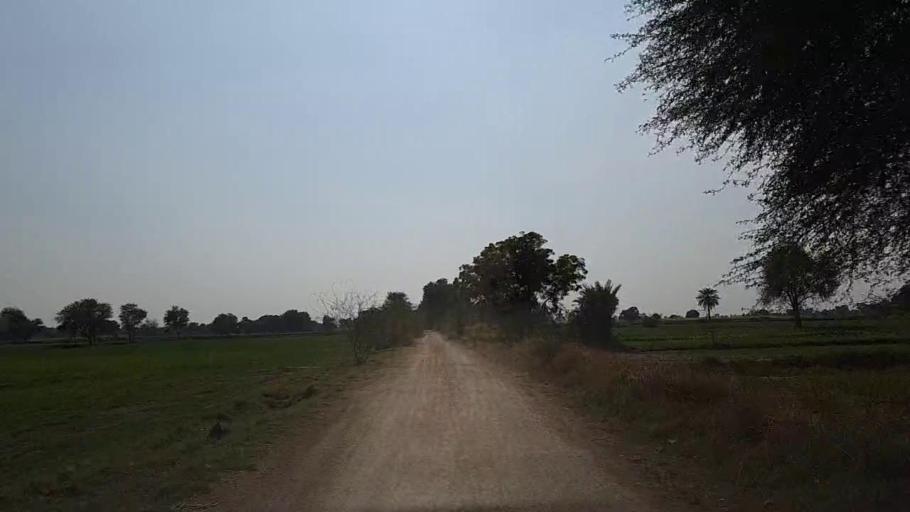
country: PK
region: Sindh
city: Nawabshah
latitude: 26.2551
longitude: 68.4899
